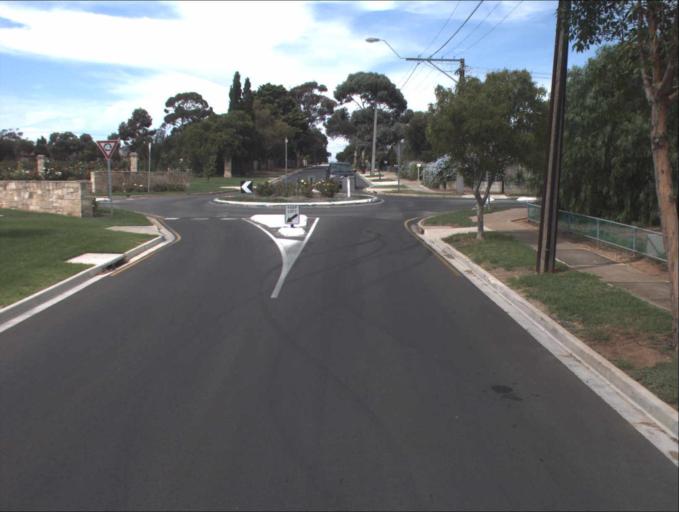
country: AU
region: South Australia
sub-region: Port Adelaide Enfield
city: Enfield
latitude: -34.8597
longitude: 138.6121
